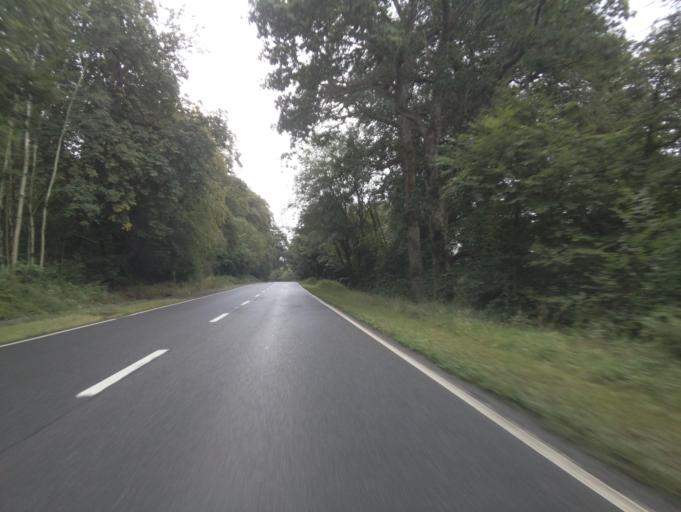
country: GB
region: Scotland
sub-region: Dumfries and Galloway
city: Moffat
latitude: 55.2384
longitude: -3.4618
